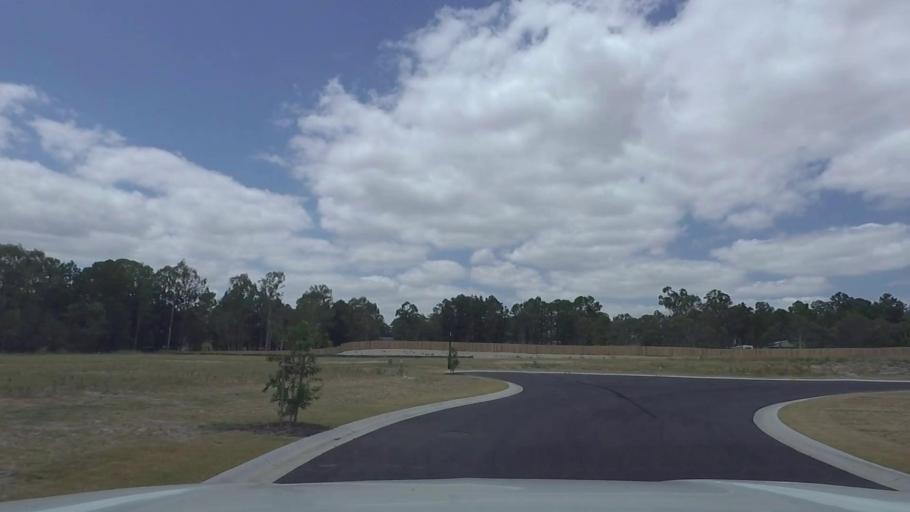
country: AU
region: Queensland
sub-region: Logan
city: North Maclean
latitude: -27.7409
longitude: 152.9528
